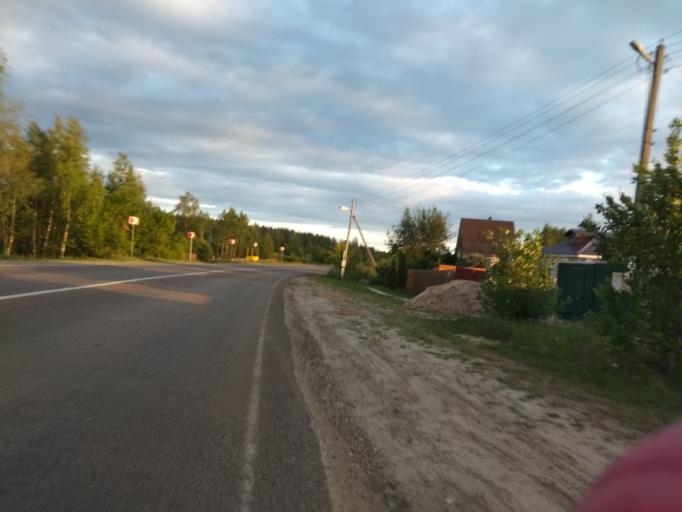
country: RU
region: Moskovskaya
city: Kerva
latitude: 55.5877
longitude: 39.7010
